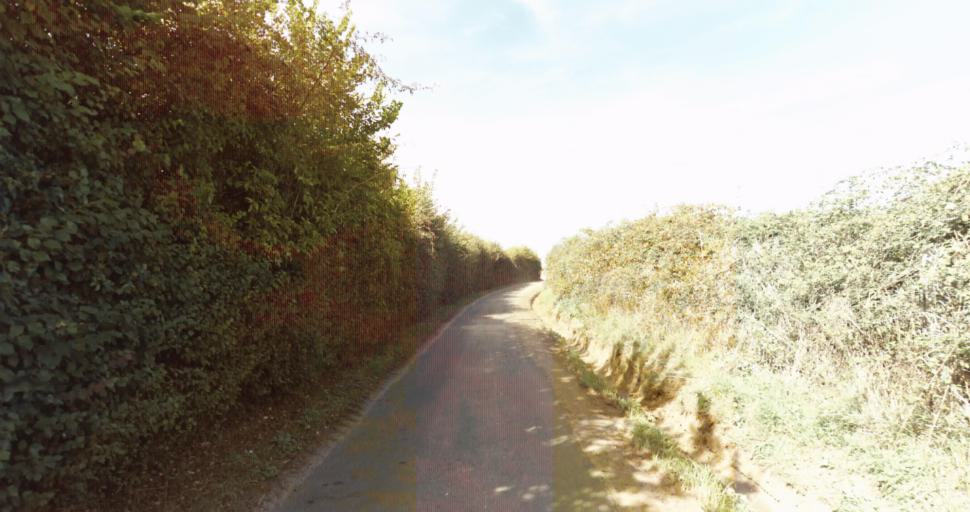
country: FR
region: Lower Normandy
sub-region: Departement de l'Orne
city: Gace
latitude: 48.7125
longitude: 0.2209
